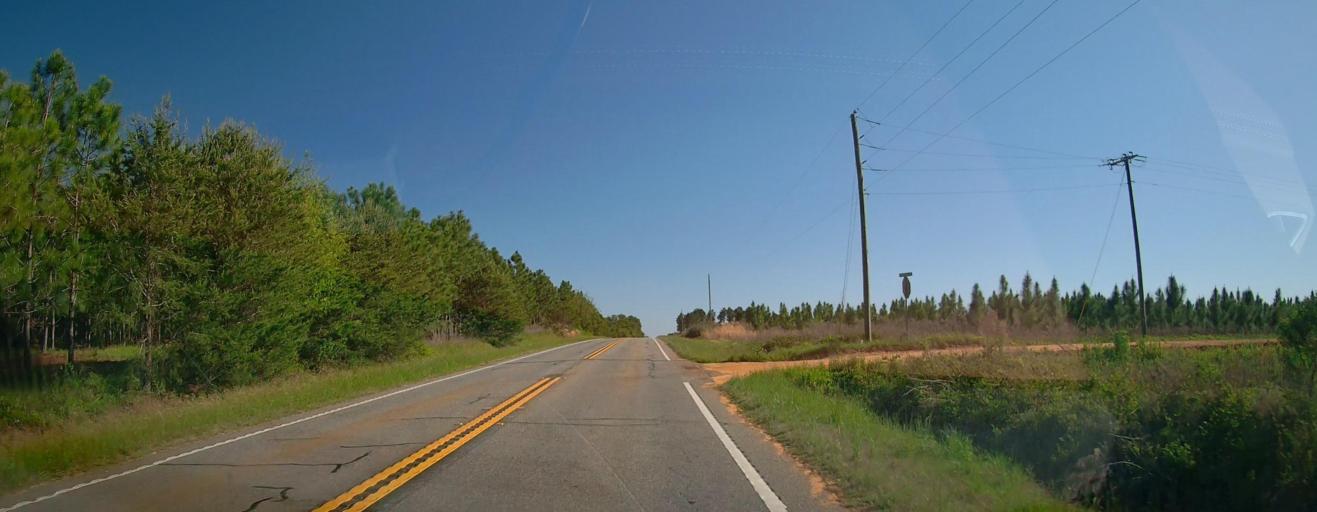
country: US
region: Georgia
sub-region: Wilcox County
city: Rochelle
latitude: 31.8363
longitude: -83.4890
